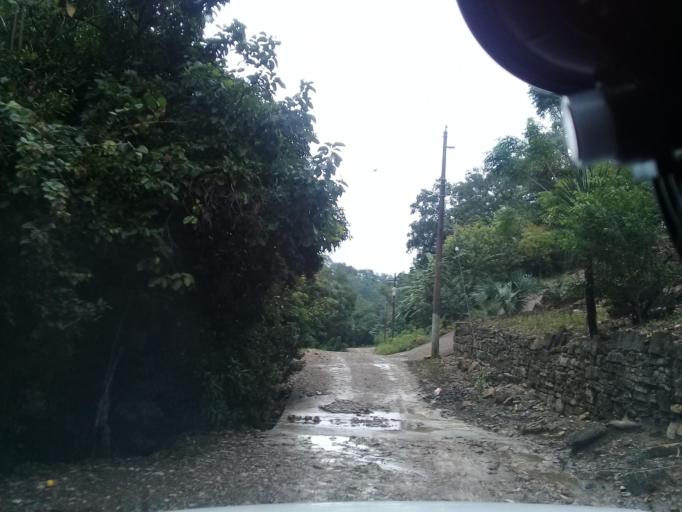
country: MX
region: Veracruz
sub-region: Chalma
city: San Pedro Coyutla
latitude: 21.2373
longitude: -98.4371
